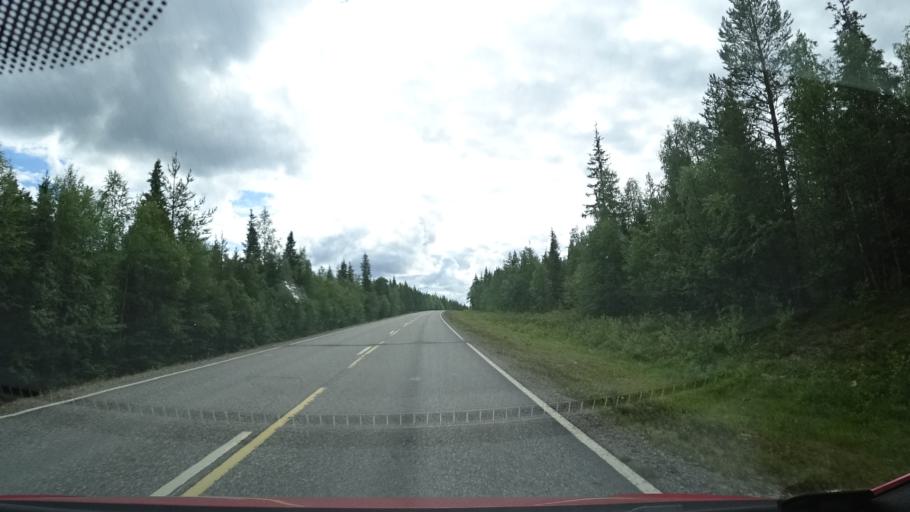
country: FI
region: Lapland
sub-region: Tunturi-Lappi
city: Kittilae
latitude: 67.5590
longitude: 24.9223
